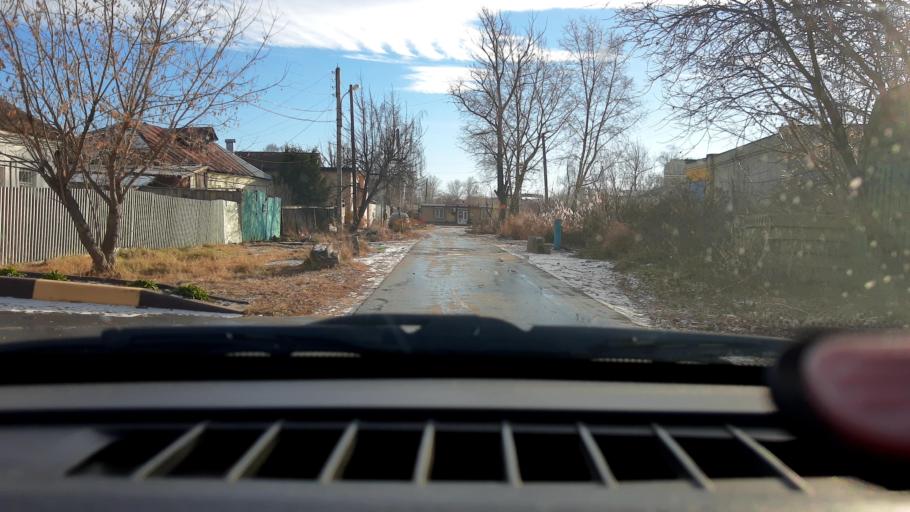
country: RU
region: Nizjnij Novgorod
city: Gorbatovka
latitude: 56.2941
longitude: 43.8487
